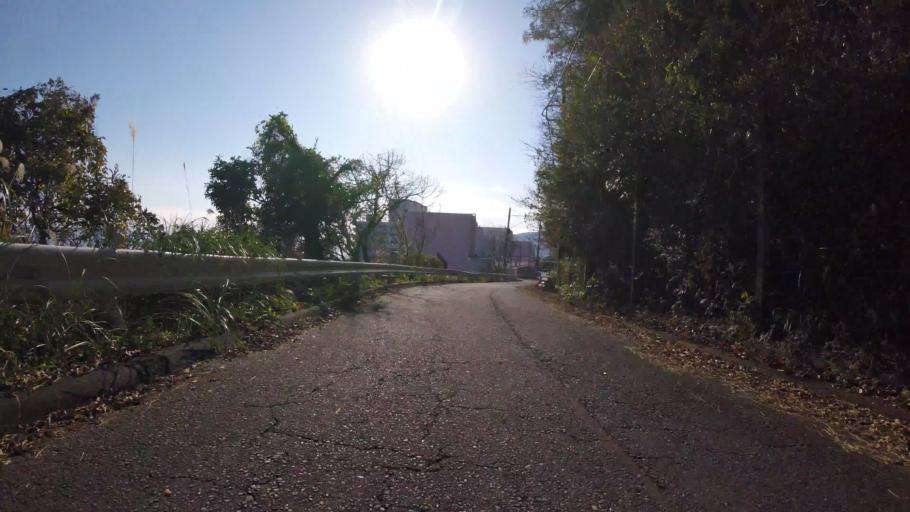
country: JP
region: Shizuoka
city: Atami
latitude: 35.0710
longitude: 139.0776
